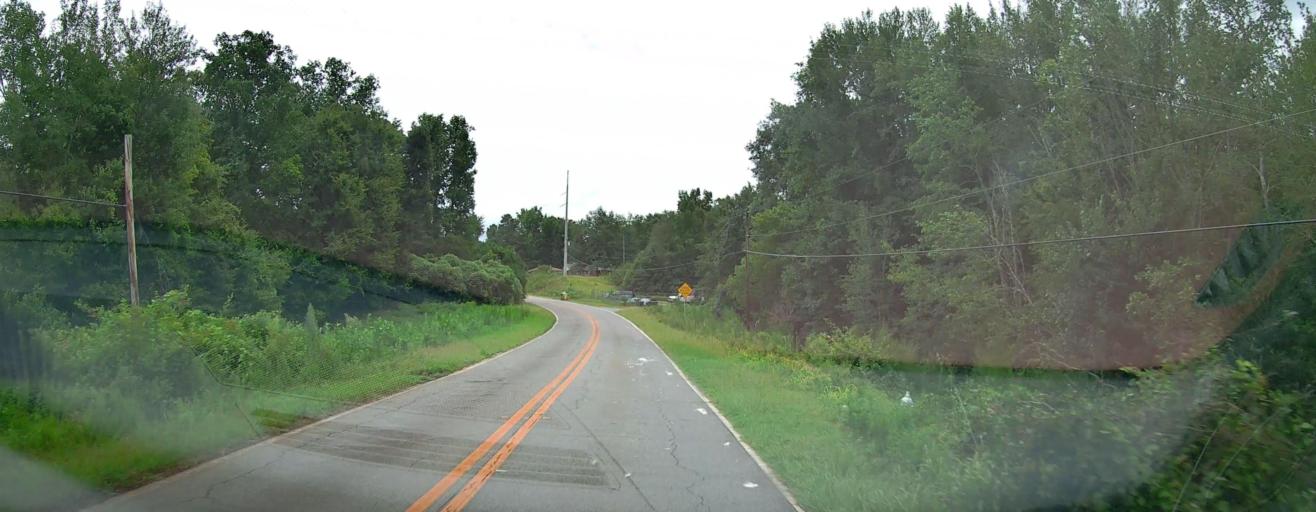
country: US
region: Georgia
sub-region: Bibb County
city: Macon
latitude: 32.8008
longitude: -83.5326
